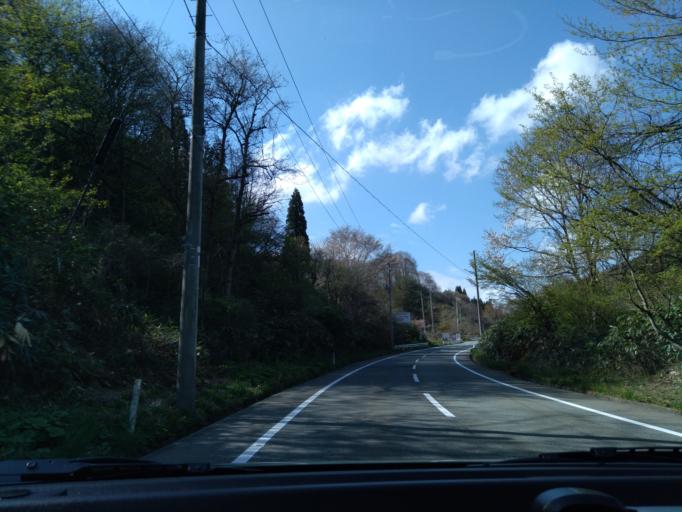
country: JP
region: Akita
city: Akita
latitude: 39.6929
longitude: 140.2226
